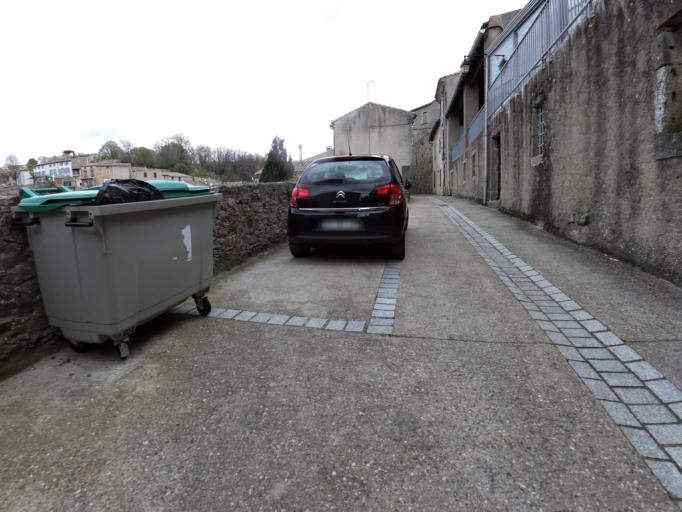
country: FR
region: Languedoc-Roussillon
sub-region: Departement de l'Aude
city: Alzonne
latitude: 43.3590
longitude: 2.1683
